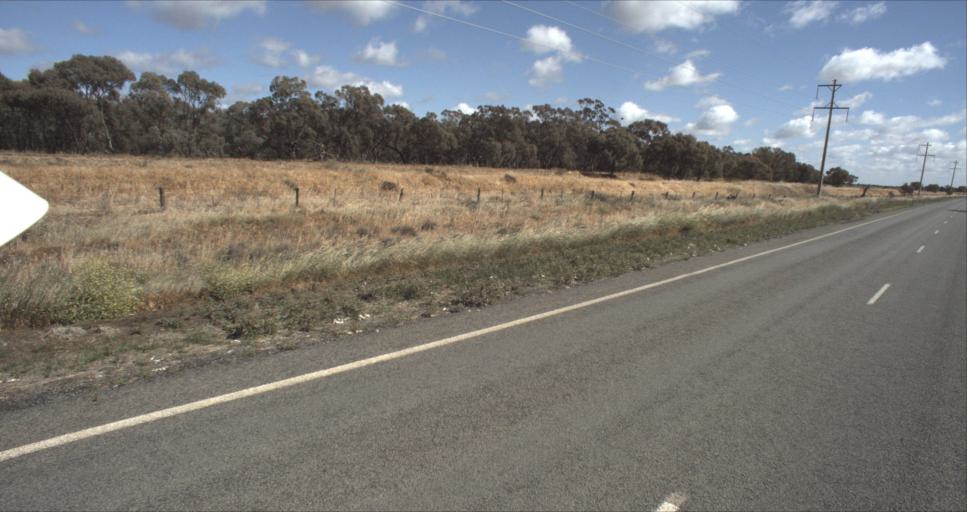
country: AU
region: New South Wales
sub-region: Murrumbidgee Shire
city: Darlington Point
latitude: -34.5460
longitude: 146.1713
